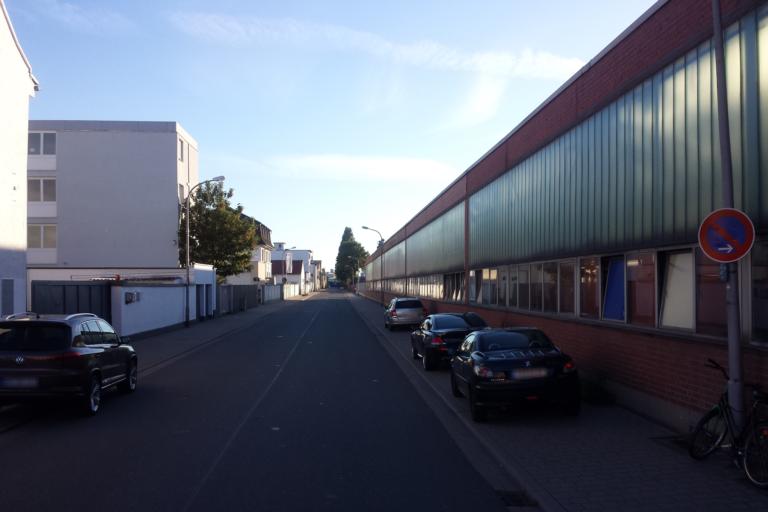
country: DE
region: Baden-Wuerttemberg
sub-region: Karlsruhe Region
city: Mannheim
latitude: 49.5112
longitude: 8.4658
